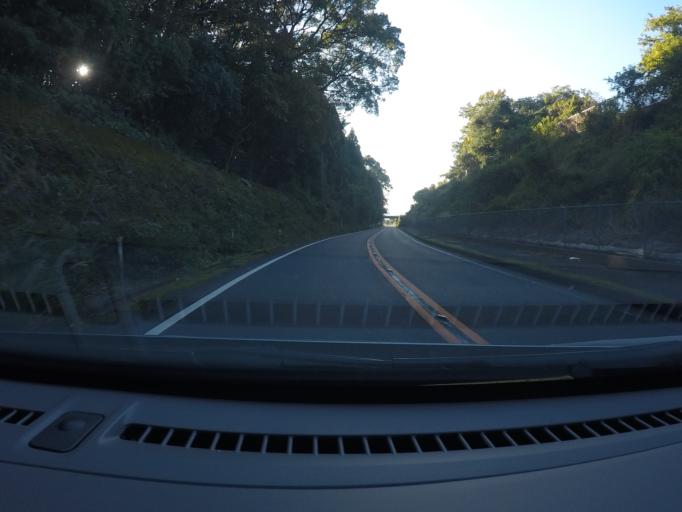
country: JP
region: Kumamoto
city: Minamata
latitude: 32.1620
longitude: 130.3733
